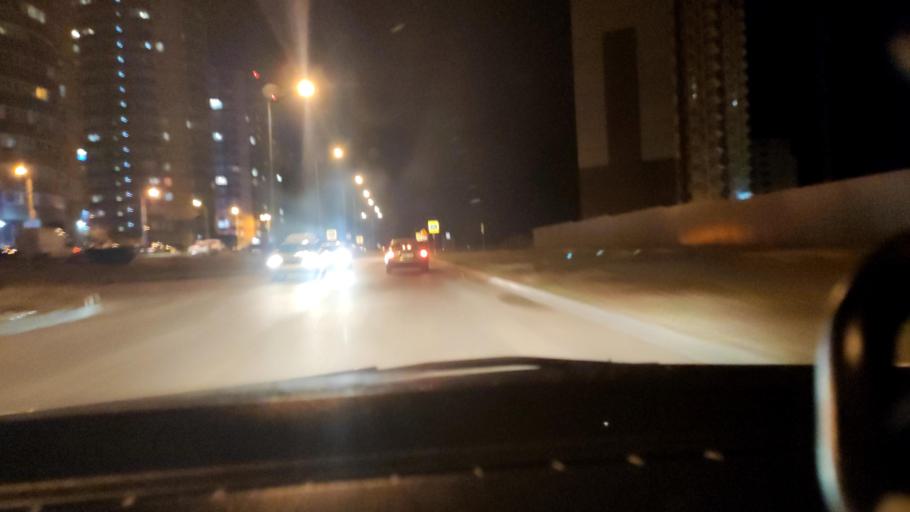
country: RU
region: Voronezj
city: Shilovo
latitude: 51.5683
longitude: 39.1224
